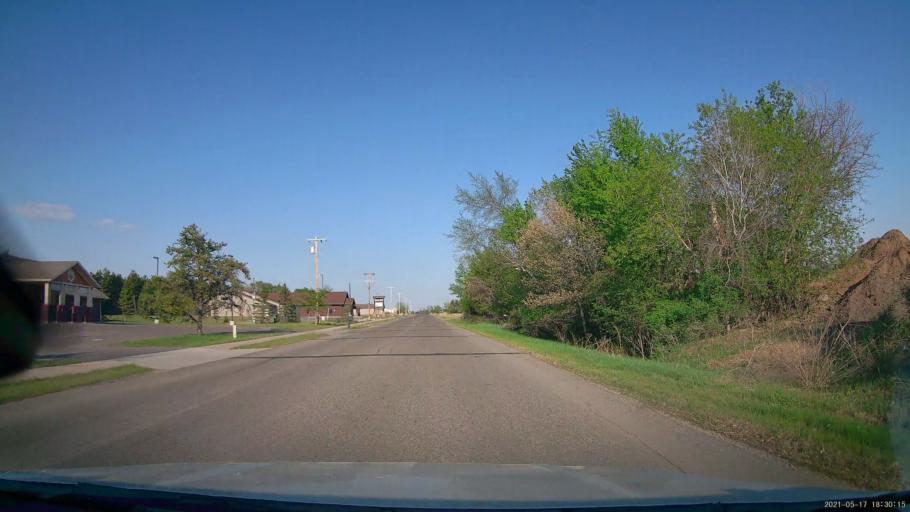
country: US
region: Minnesota
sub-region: Hubbard County
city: Park Rapids
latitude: 46.9249
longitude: -95.0414
